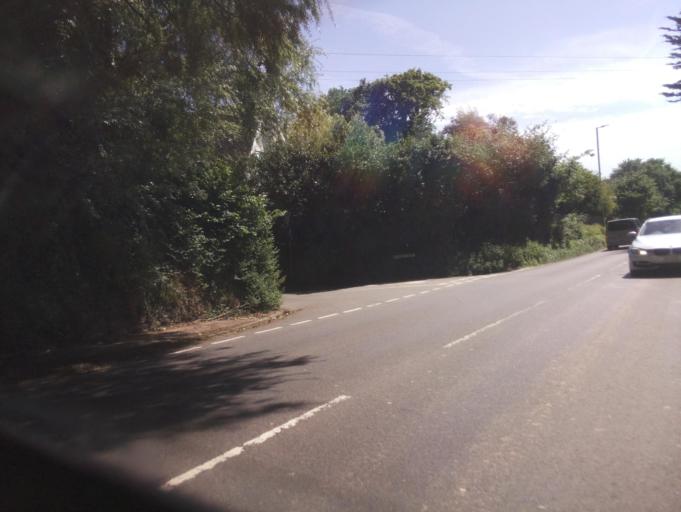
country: GB
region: England
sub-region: Devon
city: Topsham
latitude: 50.6714
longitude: -3.4393
